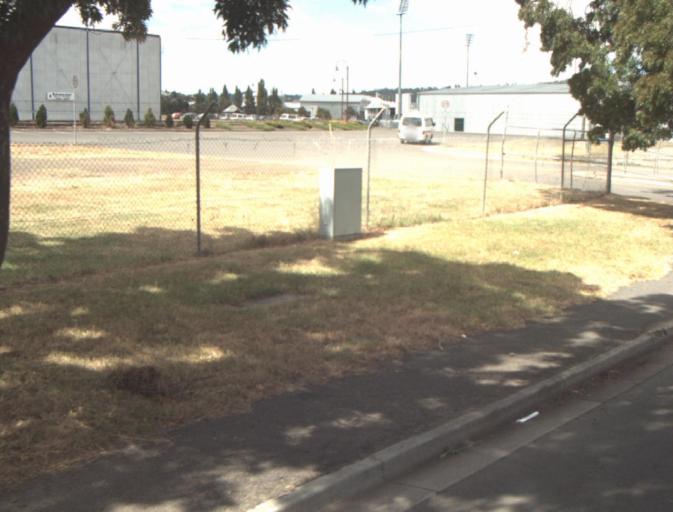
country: AU
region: Tasmania
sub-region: Launceston
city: Launceston
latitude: -41.4221
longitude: 147.1403
